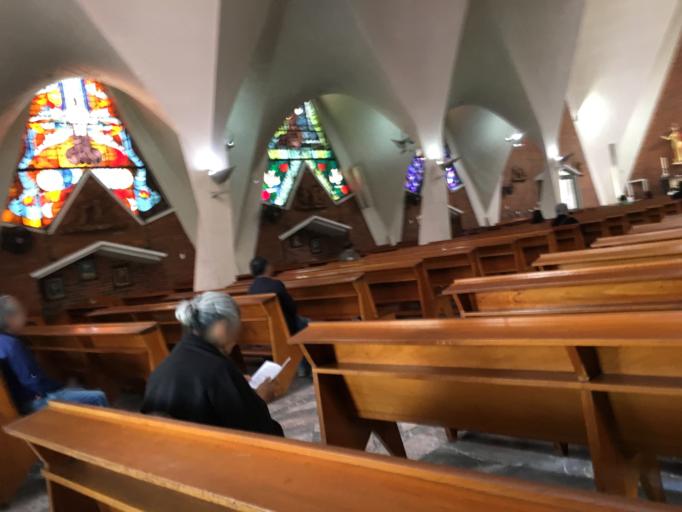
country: MX
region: Mexico City
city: Colonia del Valle
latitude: 19.3793
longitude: -99.1573
